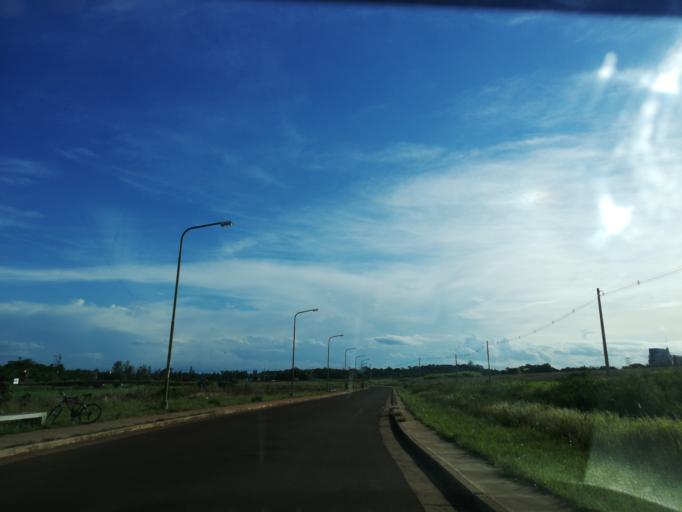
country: AR
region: Misiones
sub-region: Departamento de Capital
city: Posadas
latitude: -27.3924
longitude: -55.9549
